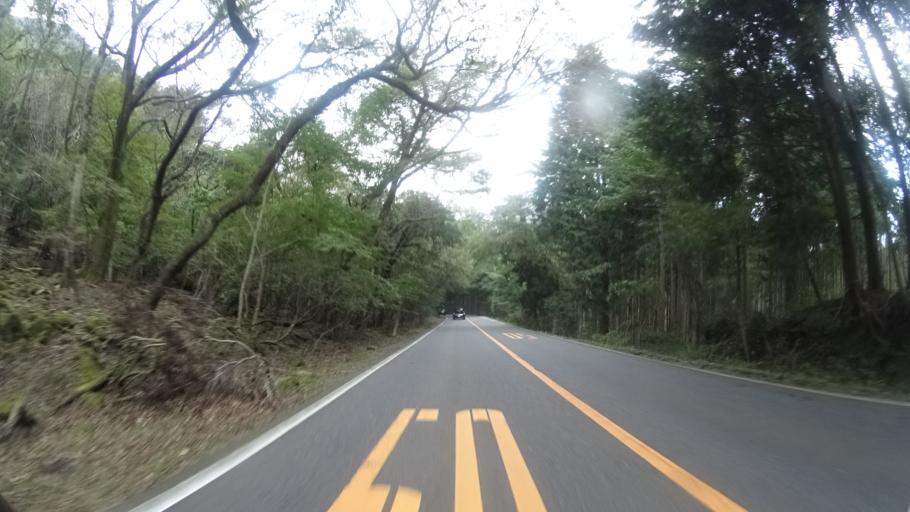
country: JP
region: Oita
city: Beppu
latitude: 33.2710
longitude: 131.4090
